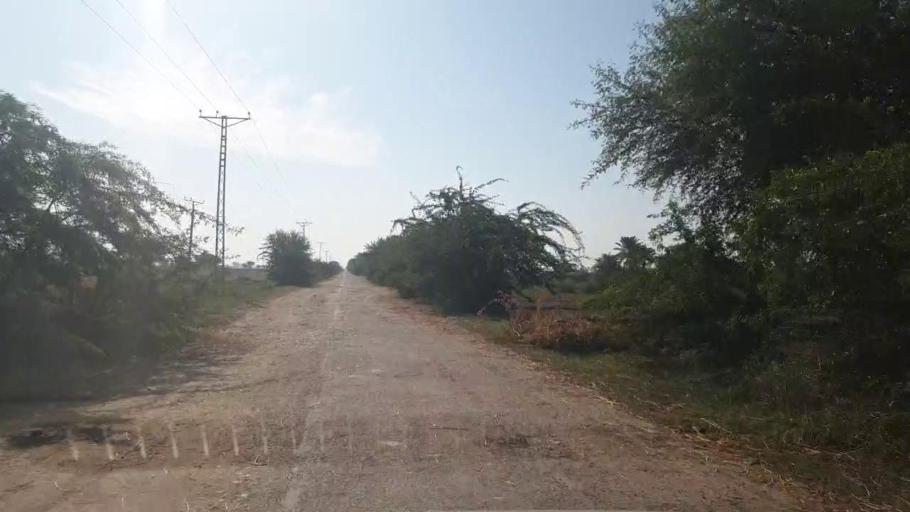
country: PK
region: Sindh
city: Talhar
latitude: 24.9199
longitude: 68.8143
